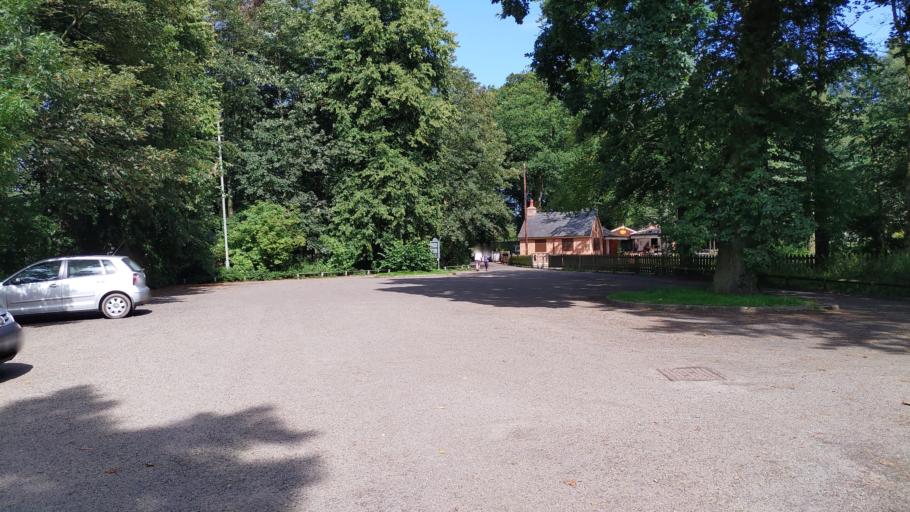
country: GB
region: England
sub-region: Lancashire
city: Leyland
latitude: 53.6825
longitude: -2.7016
